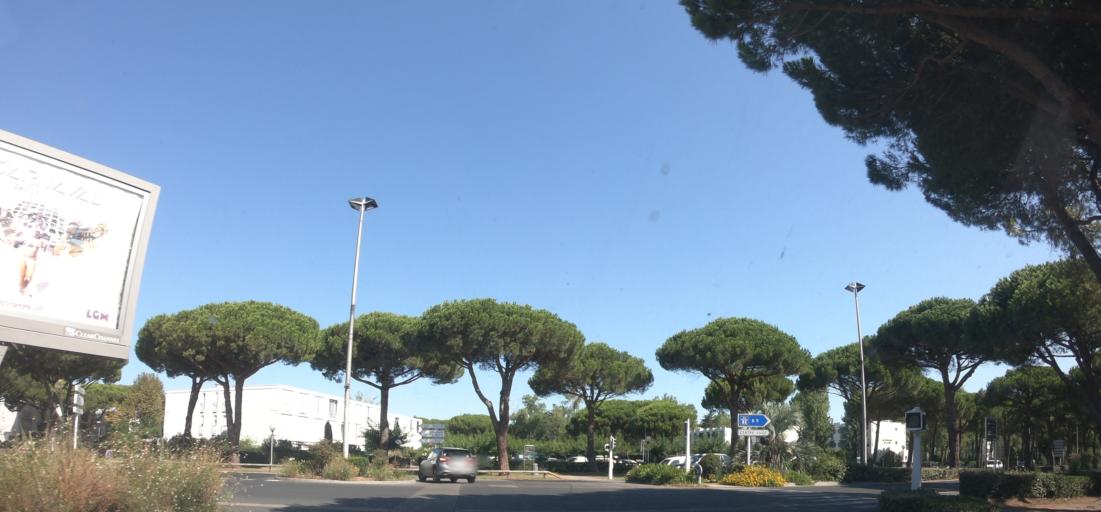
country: FR
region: Languedoc-Roussillon
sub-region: Departement de l'Herault
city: La Grande-Motte
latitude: 43.5608
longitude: 4.0776
